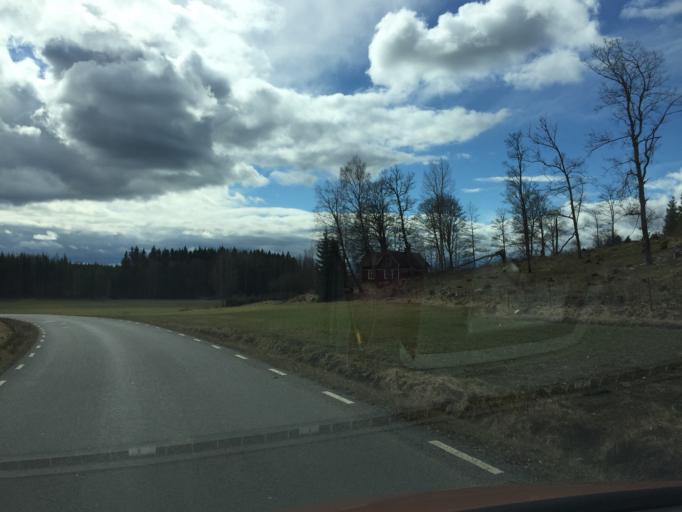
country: SE
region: Soedermanland
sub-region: Nykopings Kommun
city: Stigtomta
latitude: 58.9651
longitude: 16.9004
